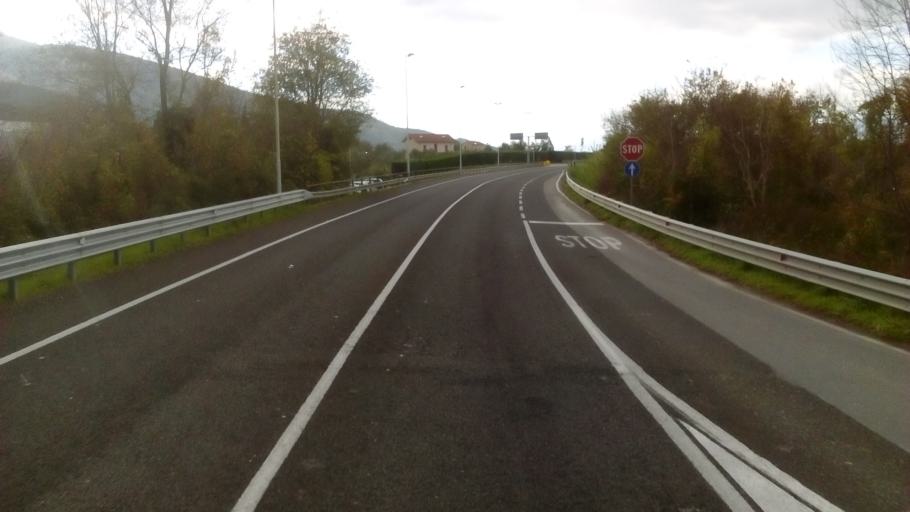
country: IT
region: Molise
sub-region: Provincia di Isernia
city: Sant'Agapito
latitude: 41.5676
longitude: 14.2058
